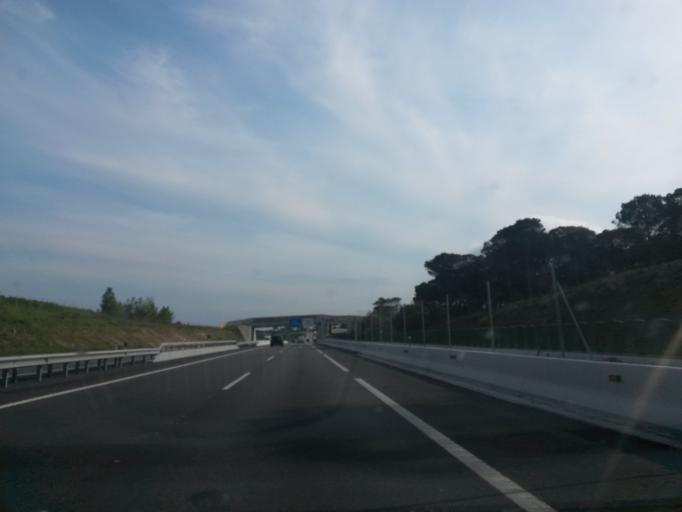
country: ES
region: Catalonia
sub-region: Provincia de Girona
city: Sils
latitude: 41.8403
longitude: 2.7599
